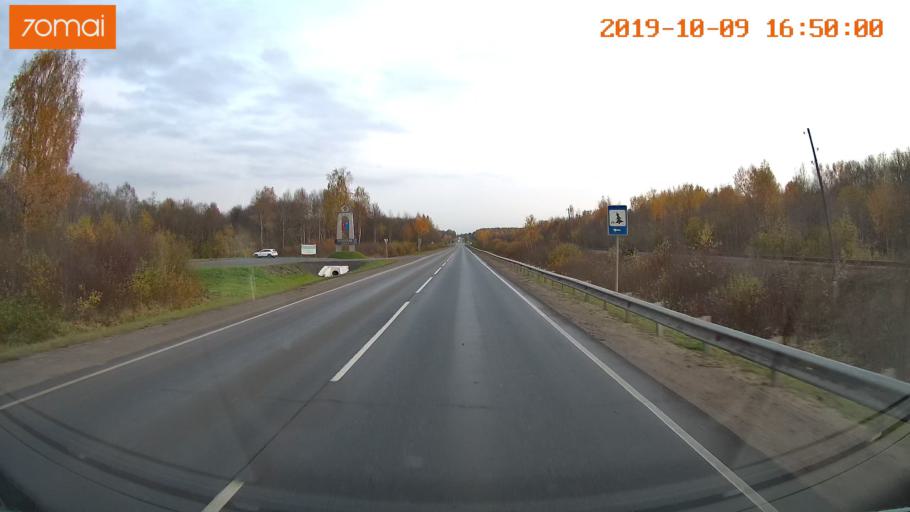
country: RU
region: Kostroma
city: Volgorechensk
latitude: 57.4069
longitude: 41.2033
